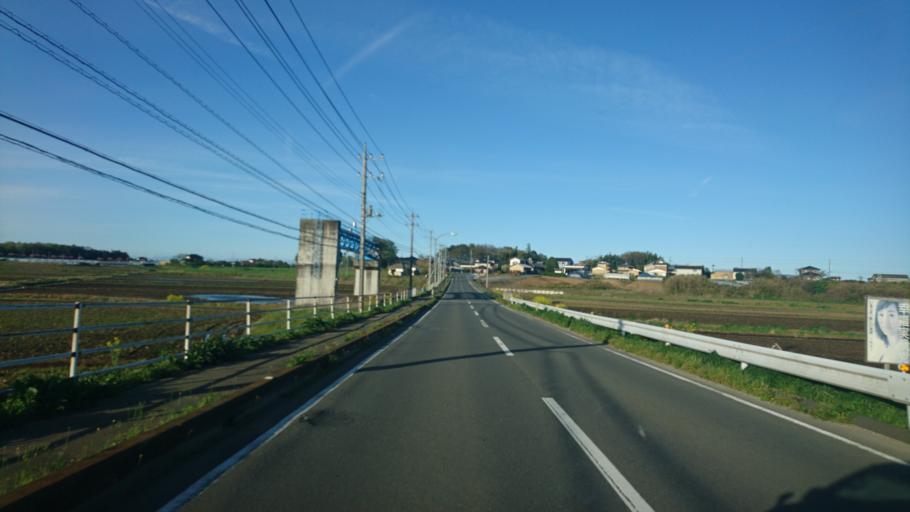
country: JP
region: Ibaraki
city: Shimodate
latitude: 36.2527
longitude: 139.9426
